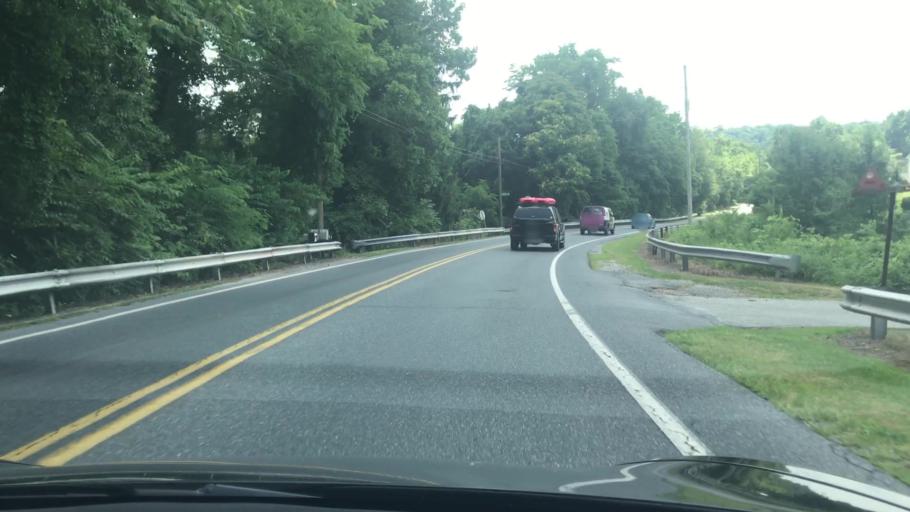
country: US
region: Pennsylvania
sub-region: York County
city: Valley Green
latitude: 40.1096
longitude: -76.7689
